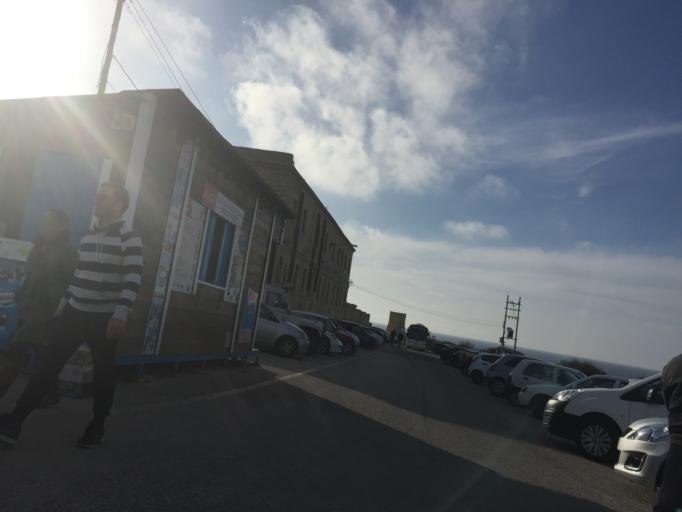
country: MT
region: L-Imgarr
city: Imgarr
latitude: 35.9308
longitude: 14.3464
